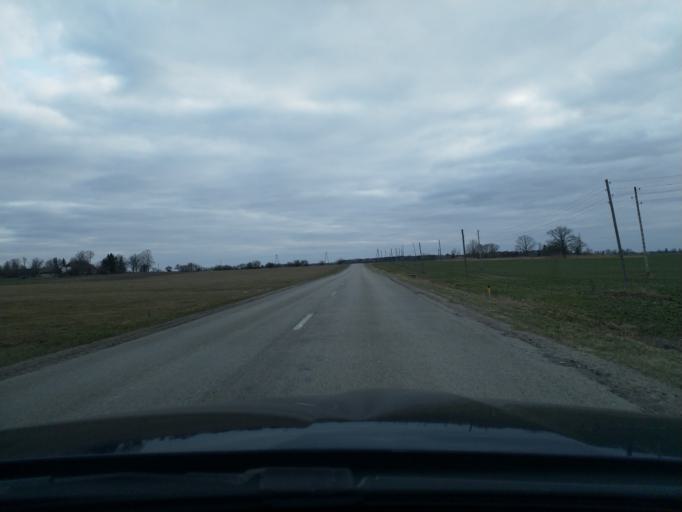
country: LV
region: Talsu Rajons
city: Sabile
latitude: 56.9490
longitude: 22.6052
